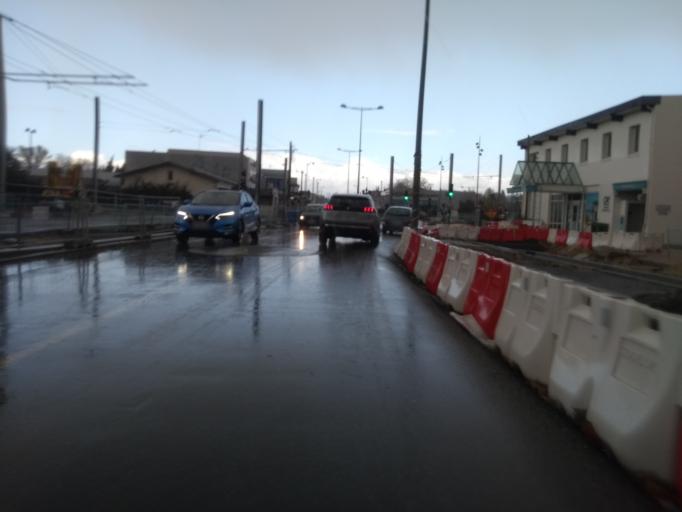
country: FR
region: Aquitaine
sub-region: Departement de la Gironde
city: Villenave-d'Ornon
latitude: 44.7824
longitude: -0.5660
